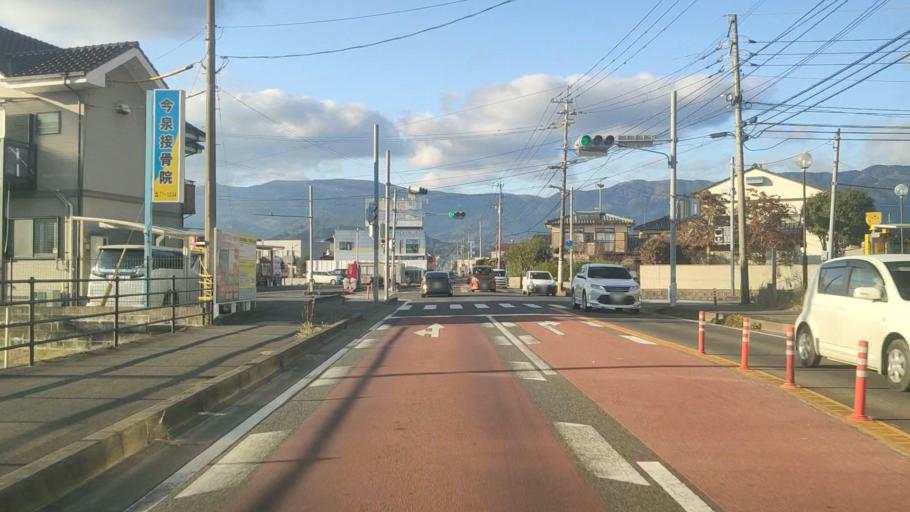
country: JP
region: Saga Prefecture
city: Saga-shi
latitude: 33.2793
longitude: 130.2135
